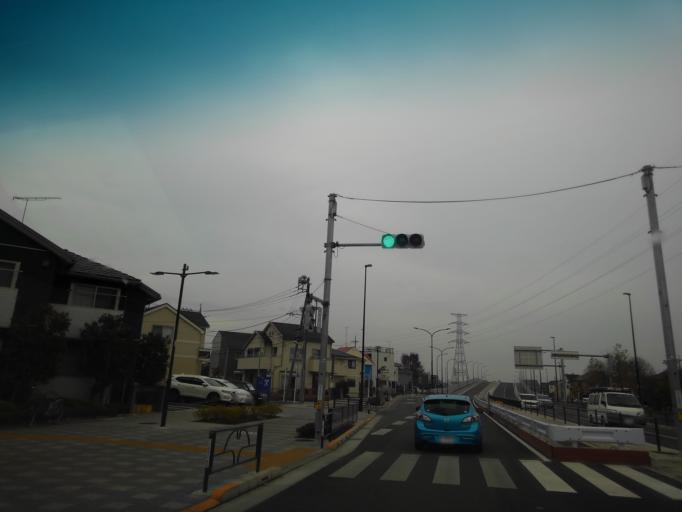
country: JP
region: Tokyo
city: Kokubunji
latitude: 35.6962
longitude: 139.4599
